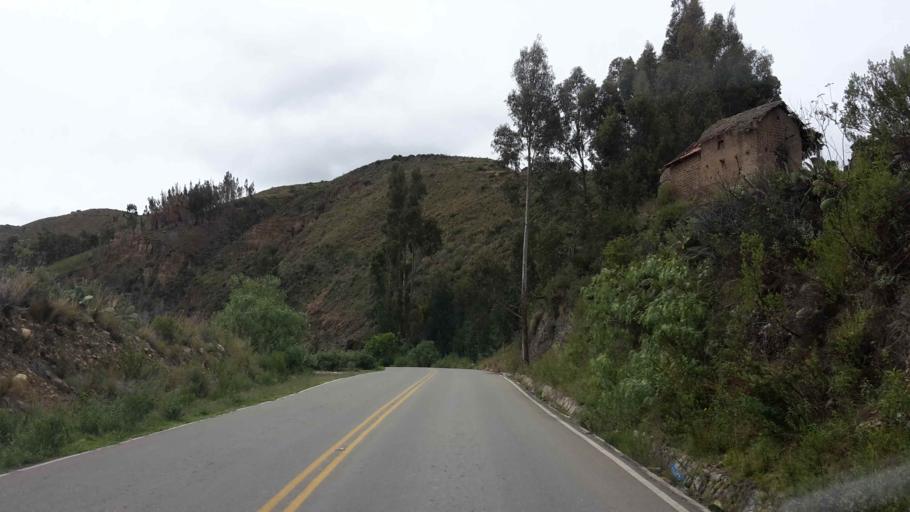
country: BO
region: Cochabamba
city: Colomi
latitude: -17.4005
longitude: -65.8002
